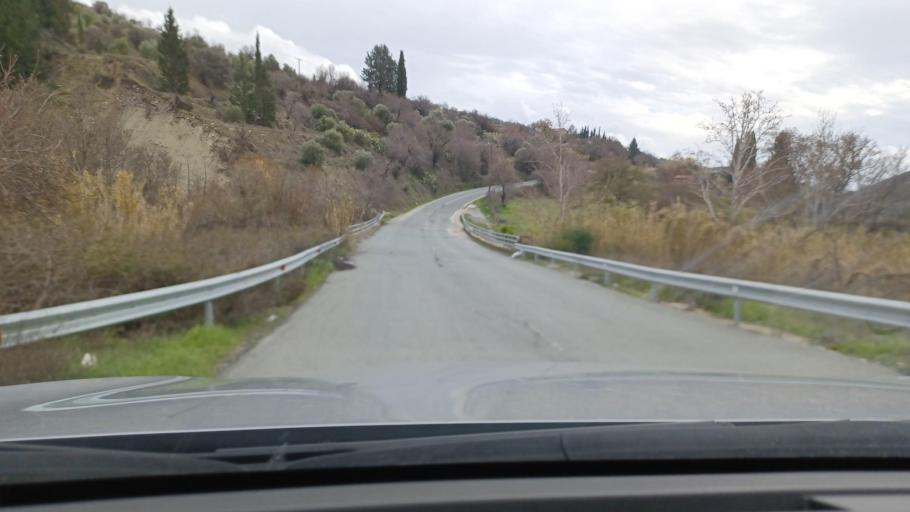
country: CY
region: Limassol
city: Pelendri
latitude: 34.8161
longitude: 32.9037
